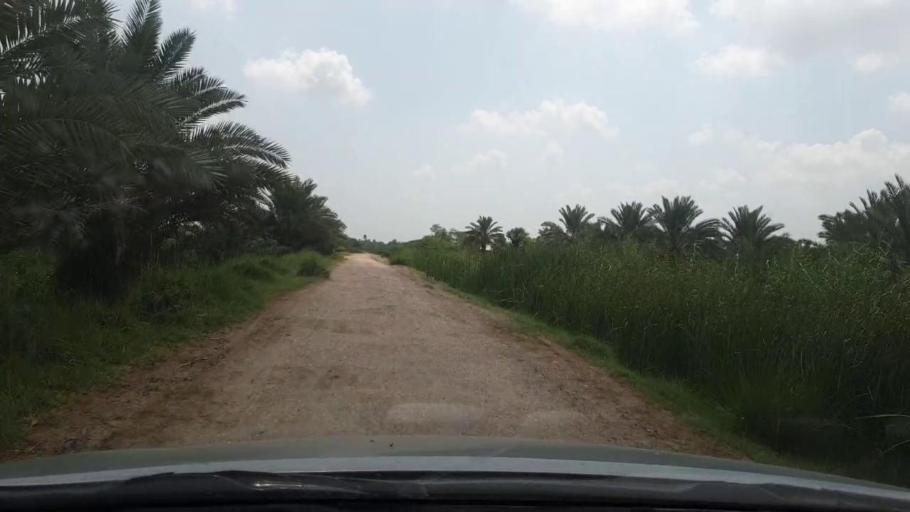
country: PK
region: Sindh
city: Kot Diji
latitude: 27.3995
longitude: 68.7364
